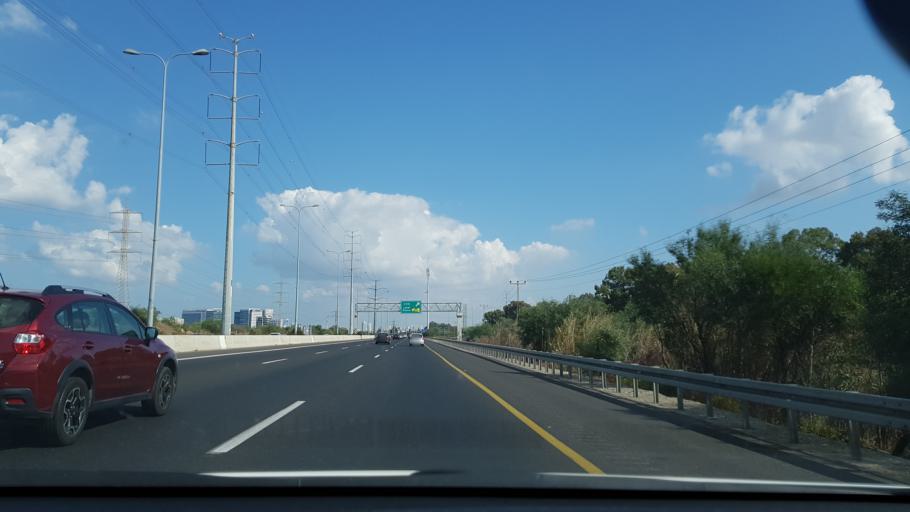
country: IL
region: Central District
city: Rishon LeZiyyon
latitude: 31.9902
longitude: 34.7980
